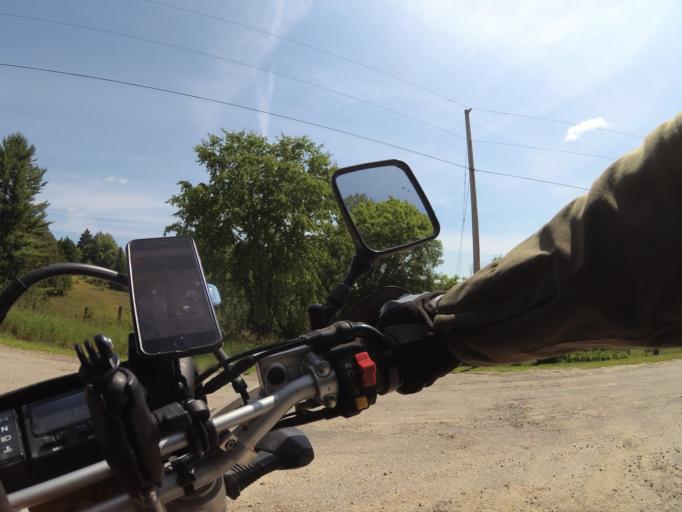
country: CA
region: Ontario
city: Skatepark
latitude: 44.7398
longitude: -76.8329
